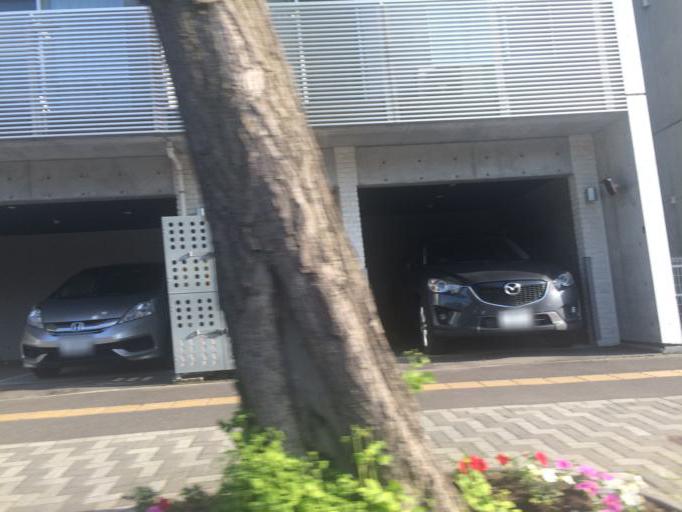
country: JP
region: Hokkaido
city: Sapporo
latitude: 43.0477
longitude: 141.3326
